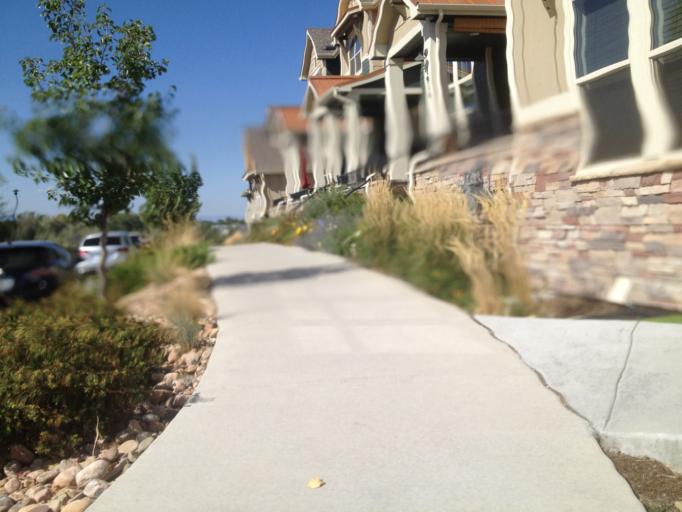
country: US
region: Colorado
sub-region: Boulder County
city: Louisville
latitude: 39.9897
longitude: -105.1333
